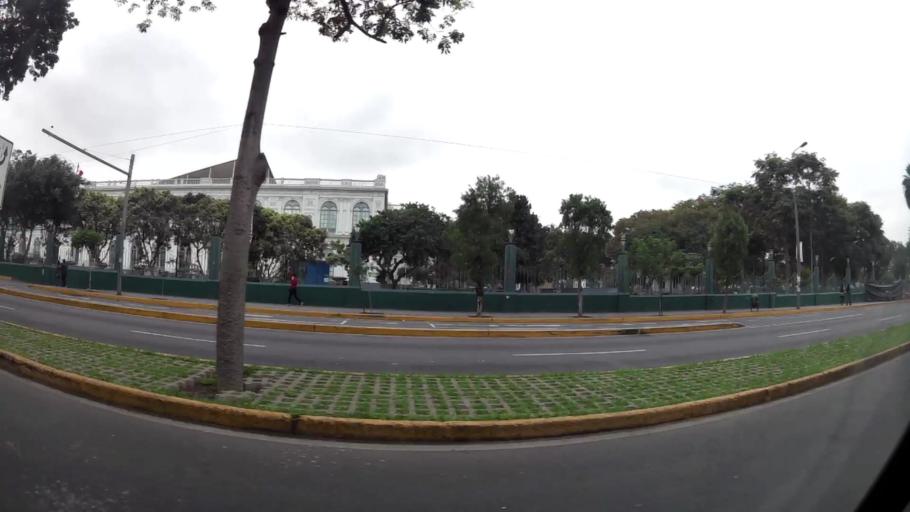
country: PE
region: Lima
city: Lima
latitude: -12.0610
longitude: -77.0378
